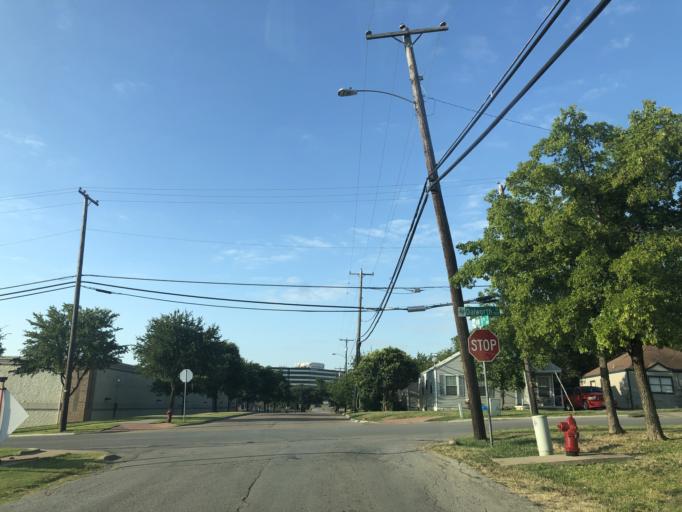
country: US
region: Texas
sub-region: Dallas County
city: Grand Prairie
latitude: 32.7448
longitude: -97.0188
